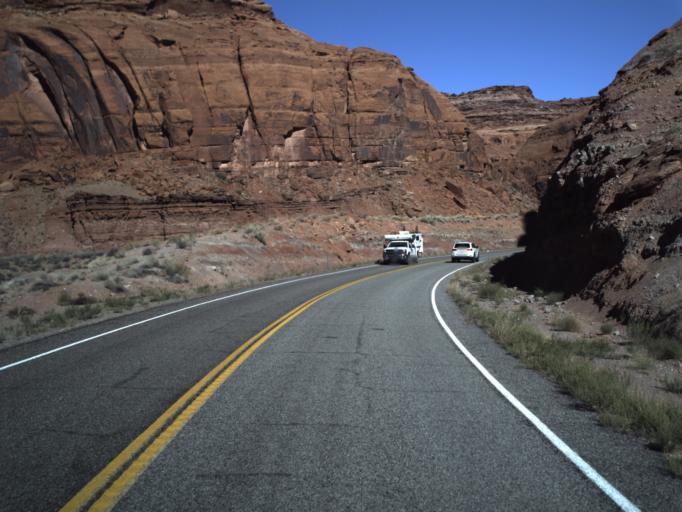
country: US
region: Utah
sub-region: San Juan County
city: Blanding
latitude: 37.9549
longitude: -110.4805
